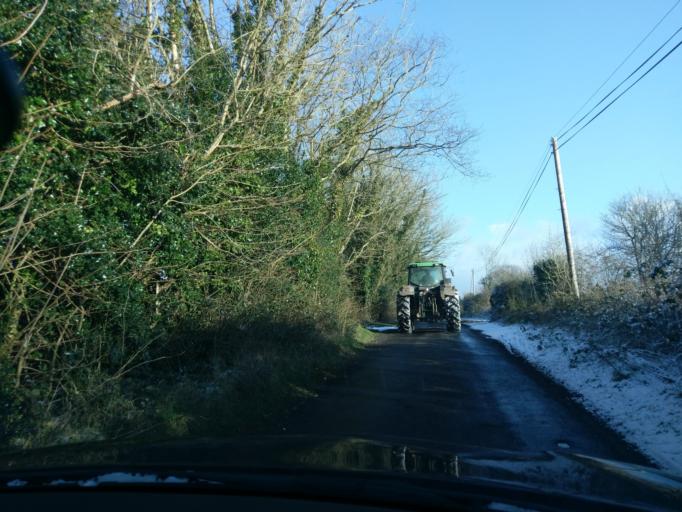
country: IE
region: Connaught
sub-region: County Galway
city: Gort
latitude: 53.1789
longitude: -8.7960
